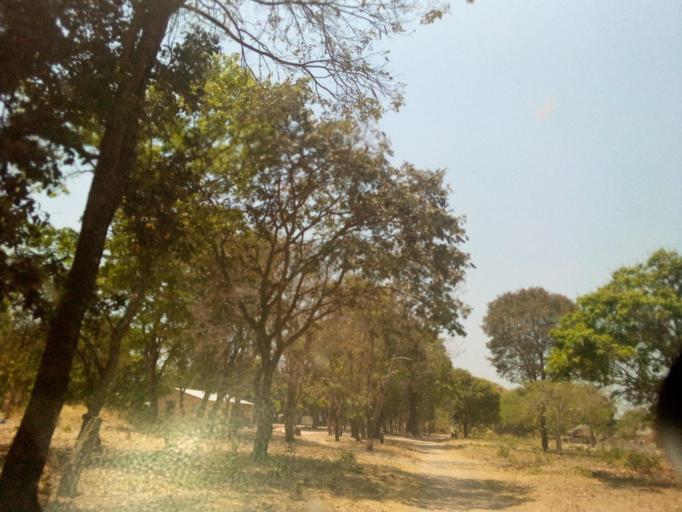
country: ZM
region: Copperbelt
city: Kataba
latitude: -12.2552
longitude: 30.3584
